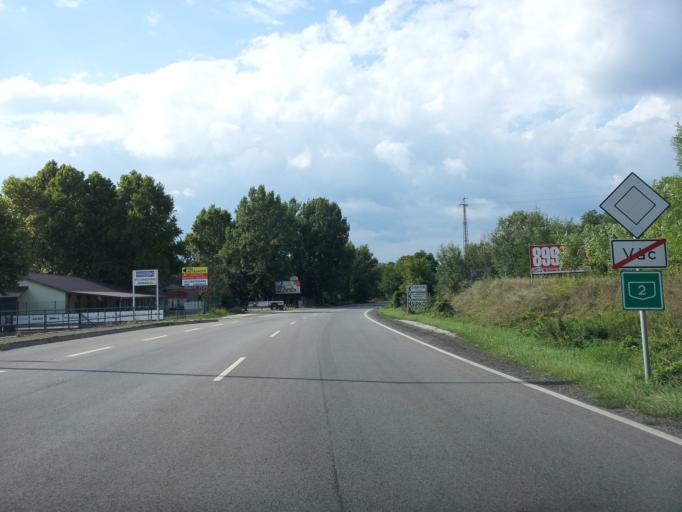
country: HU
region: Pest
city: Vac
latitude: 47.7977
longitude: 19.1088
